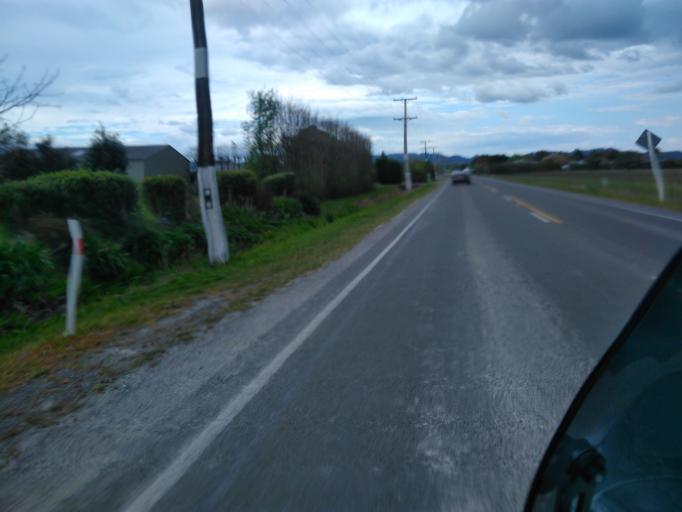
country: NZ
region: Gisborne
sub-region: Gisborne District
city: Gisborne
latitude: -38.6538
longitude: 177.9556
